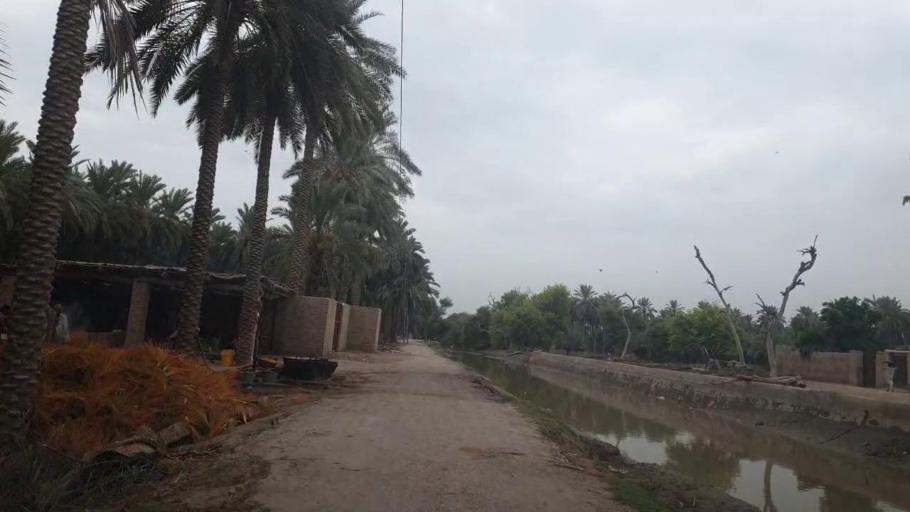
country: PK
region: Sindh
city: Khairpur
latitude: 27.6318
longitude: 68.7760
